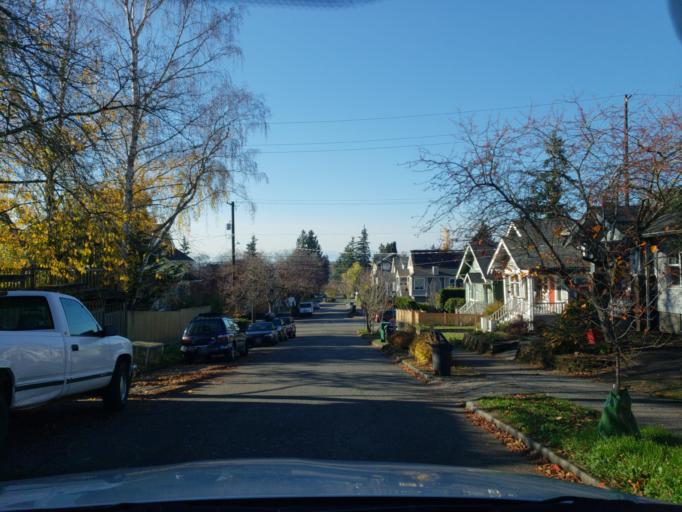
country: US
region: Washington
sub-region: King County
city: Seattle
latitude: 47.6778
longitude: -122.3597
